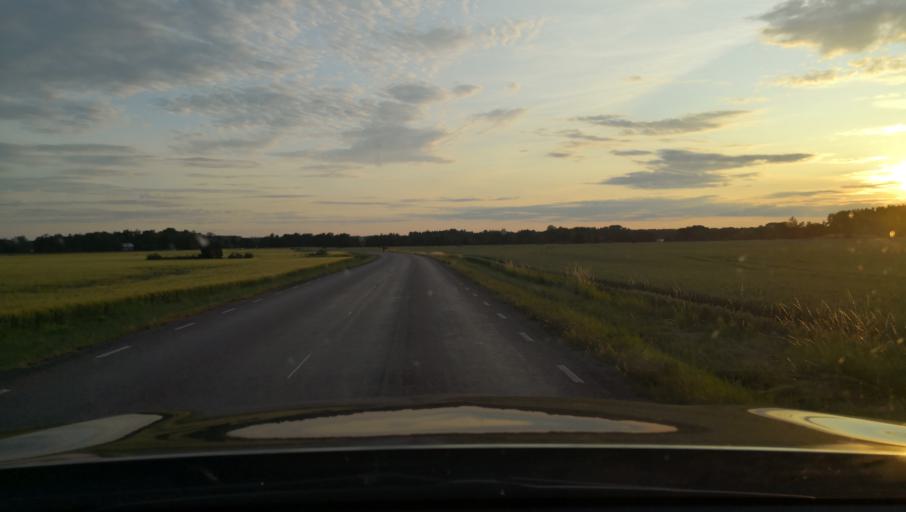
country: SE
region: Uppsala
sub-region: Uppsala Kommun
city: Vattholma
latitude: 60.0226
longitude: 17.6866
